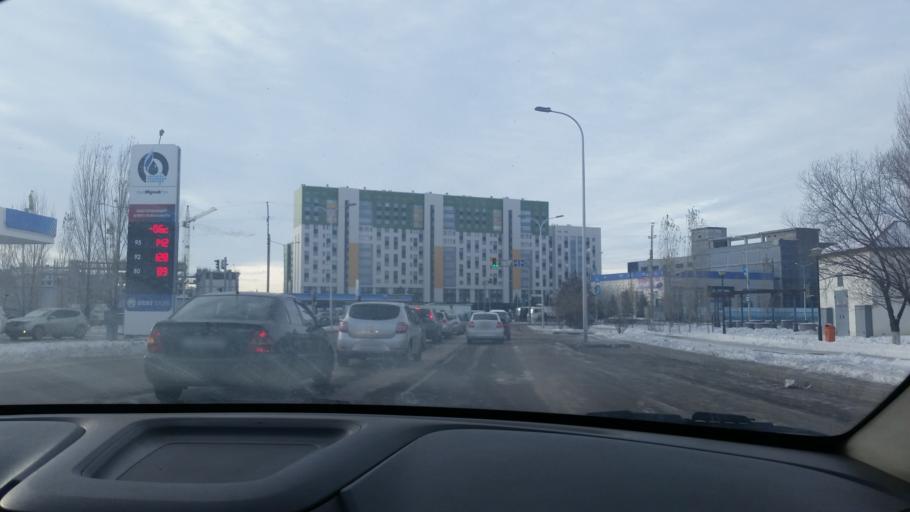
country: KZ
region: Astana Qalasy
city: Astana
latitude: 51.1462
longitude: 71.4615
